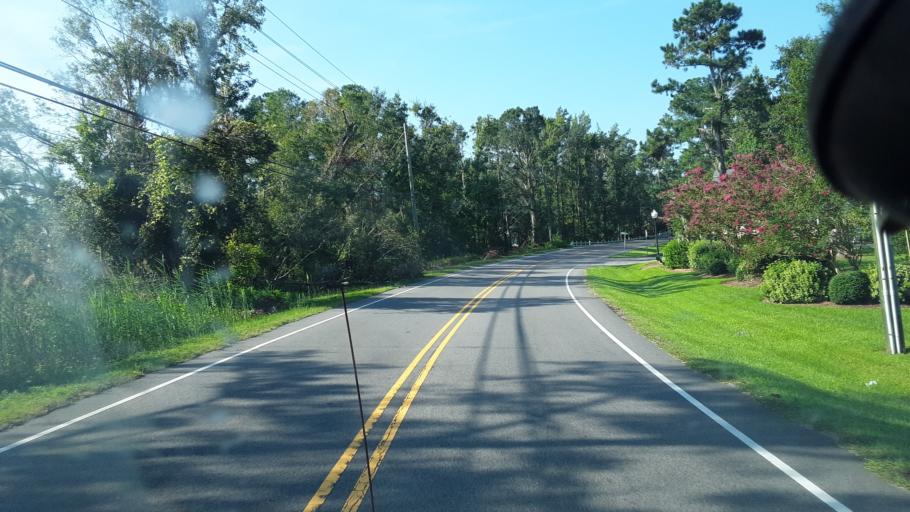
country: US
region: North Carolina
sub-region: Brunswick County
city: Belville
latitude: 34.1990
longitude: -77.9807
